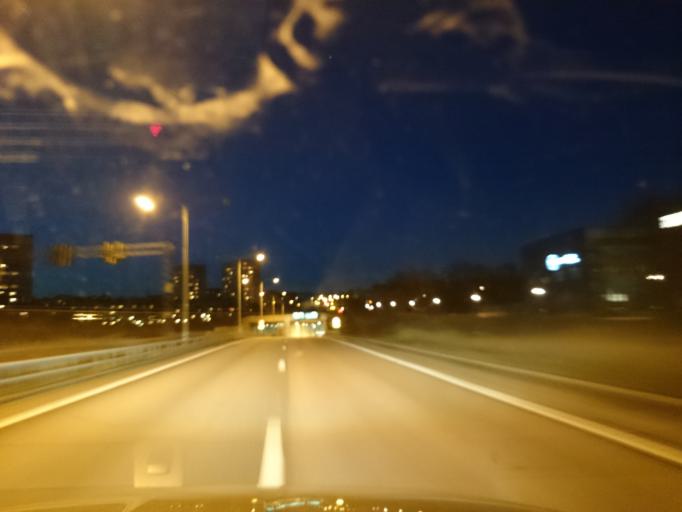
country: SE
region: Stockholm
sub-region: Stockholms Kommun
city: Arsta
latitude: 59.2897
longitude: 18.0524
